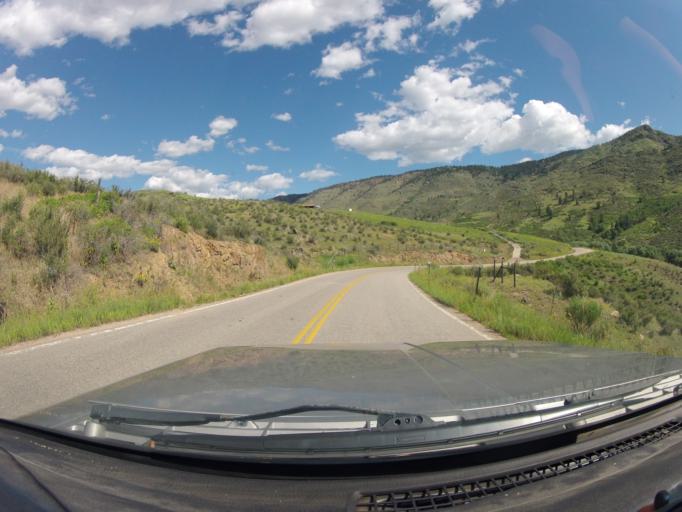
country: US
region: Colorado
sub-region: Larimer County
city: Laporte
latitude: 40.5538
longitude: -105.2910
